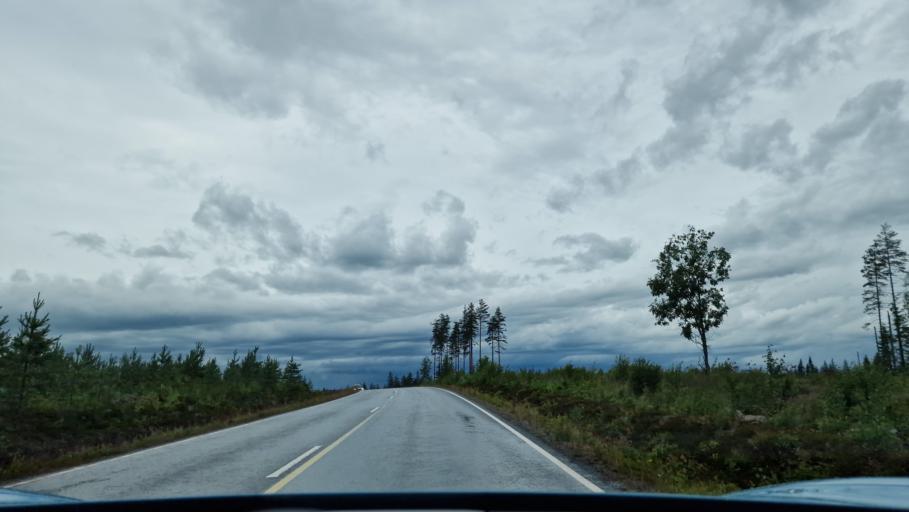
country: FI
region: Central Finland
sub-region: Saarijaervi-Viitasaari
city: Pylkoenmaeki
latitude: 62.6642
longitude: 24.5487
